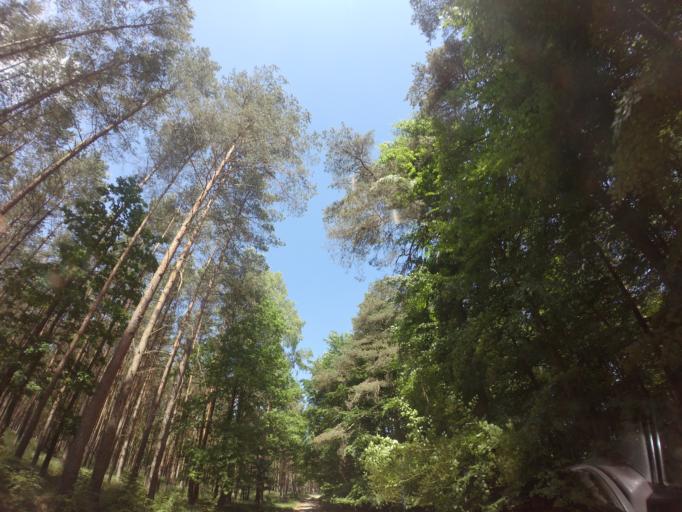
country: PL
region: West Pomeranian Voivodeship
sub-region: Powiat choszczenski
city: Drawno
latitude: 53.1634
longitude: 15.7931
